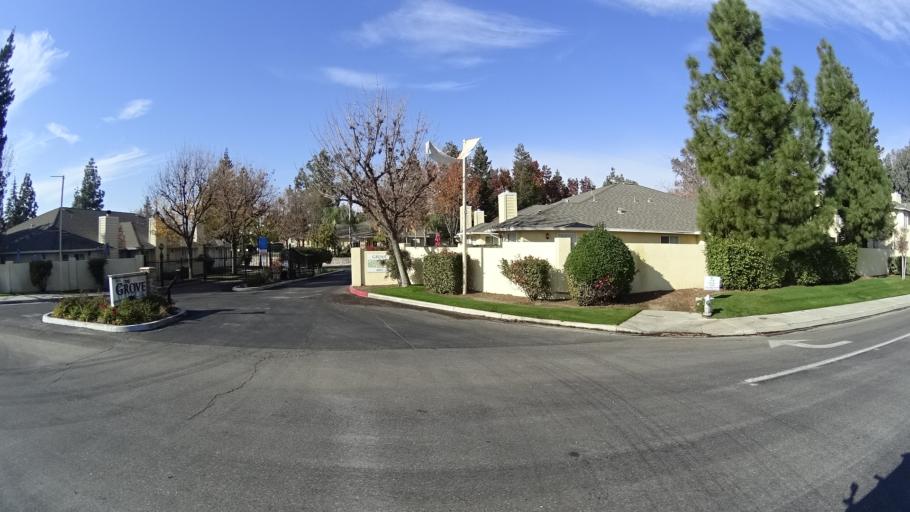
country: US
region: California
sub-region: Kern County
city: Greenacres
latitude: 35.4033
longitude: -119.0745
